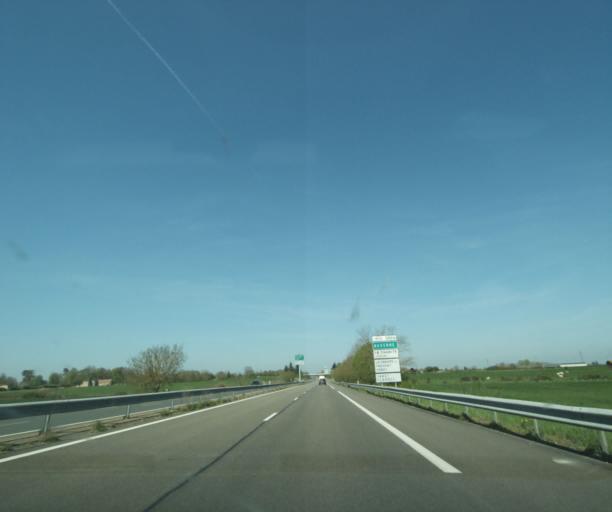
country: FR
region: Bourgogne
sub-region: Departement de la Nievre
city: La Charite-sur-Loire
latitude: 47.1803
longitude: 3.0409
